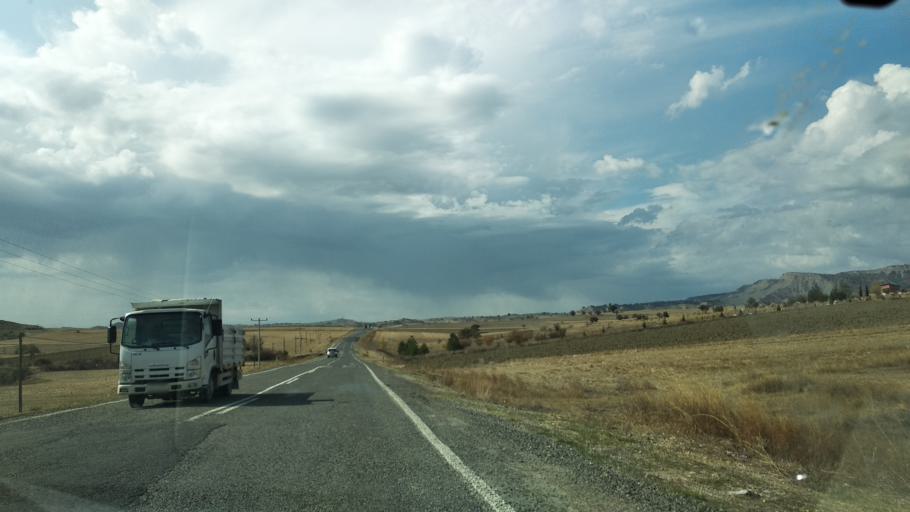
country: TR
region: Bolu
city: Seben
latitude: 40.3975
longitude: 31.5574
